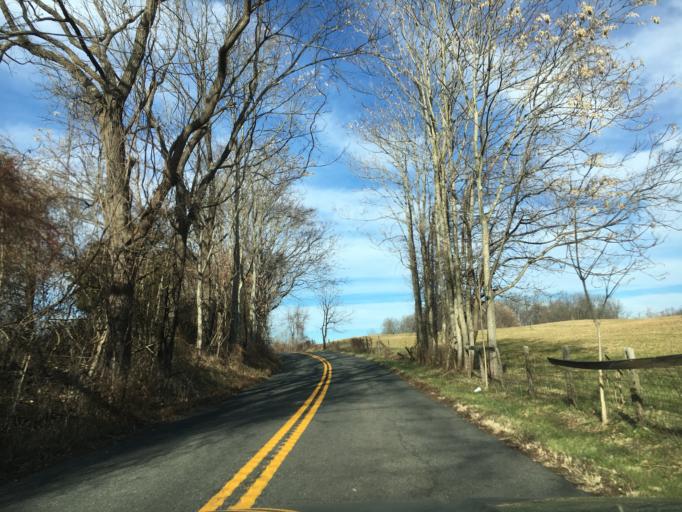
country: US
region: Virginia
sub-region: Fauquier County
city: Marshall
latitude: 38.7897
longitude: -77.9904
